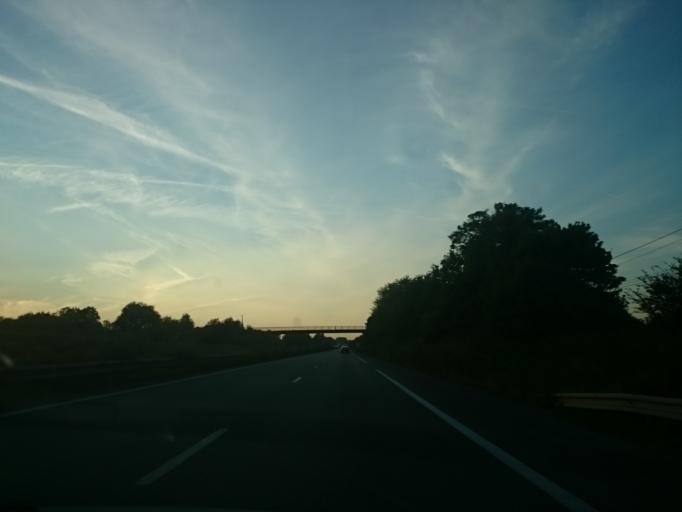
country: FR
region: Brittany
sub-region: Departement du Finistere
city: Redene
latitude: 47.8340
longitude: -3.4855
